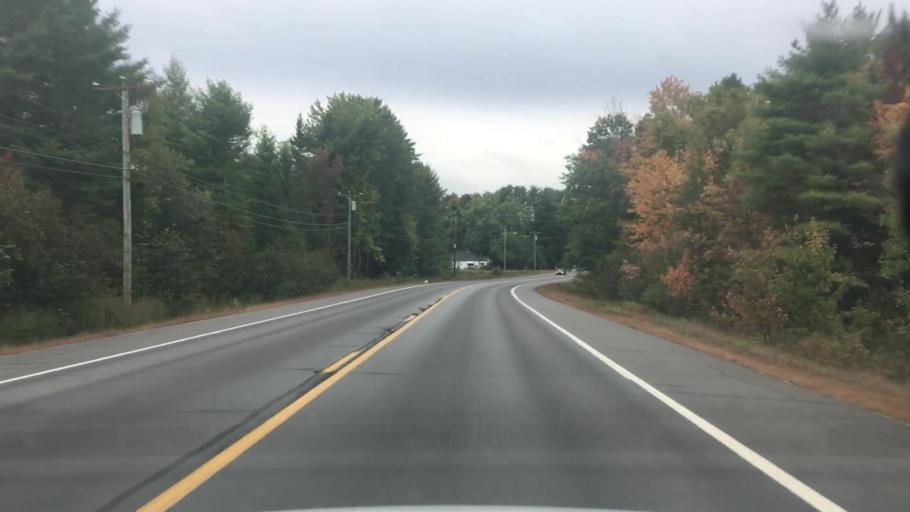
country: US
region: Maine
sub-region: Kennebec County
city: Augusta
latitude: 44.3781
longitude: -69.8000
